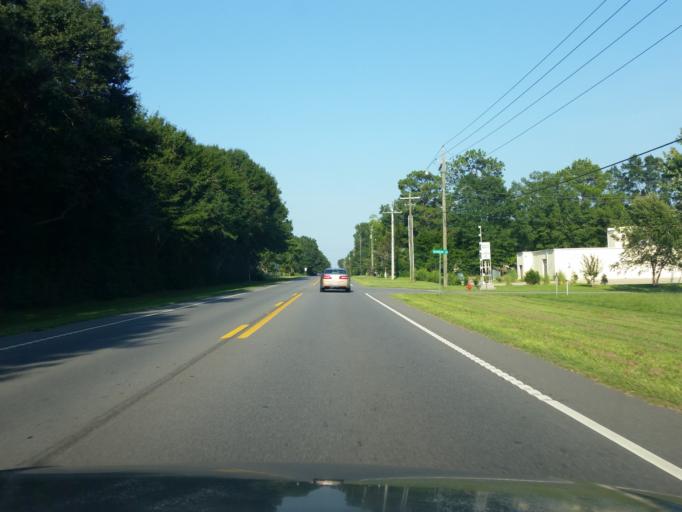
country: US
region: Alabama
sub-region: Baldwin County
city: Foley
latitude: 30.4068
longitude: -87.6635
